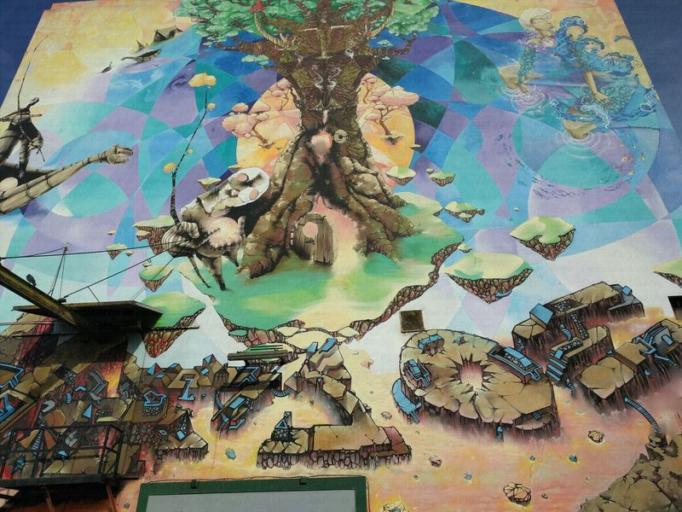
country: CL
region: Valparaiso
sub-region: Provincia de Valparaiso
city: Valparaiso
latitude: -33.0352
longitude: -71.6299
